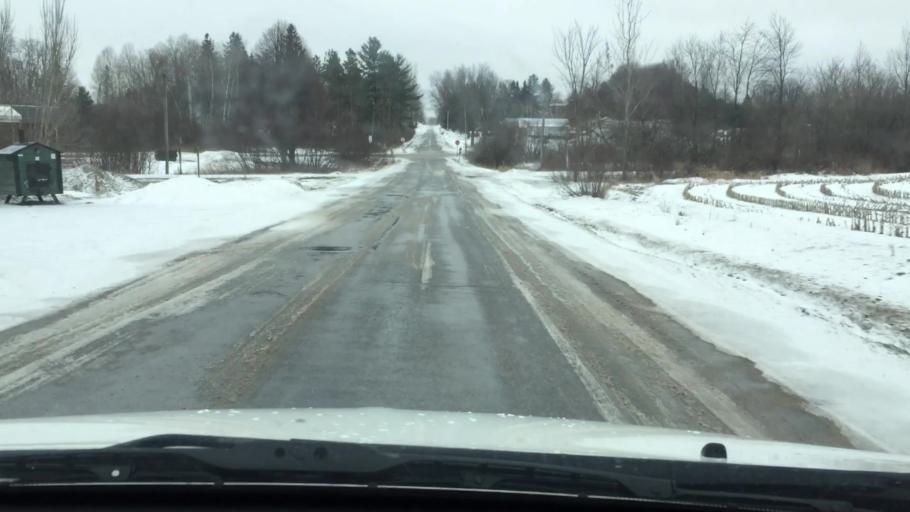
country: US
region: Michigan
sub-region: Osceola County
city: Reed City
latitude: 44.0375
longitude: -85.4538
